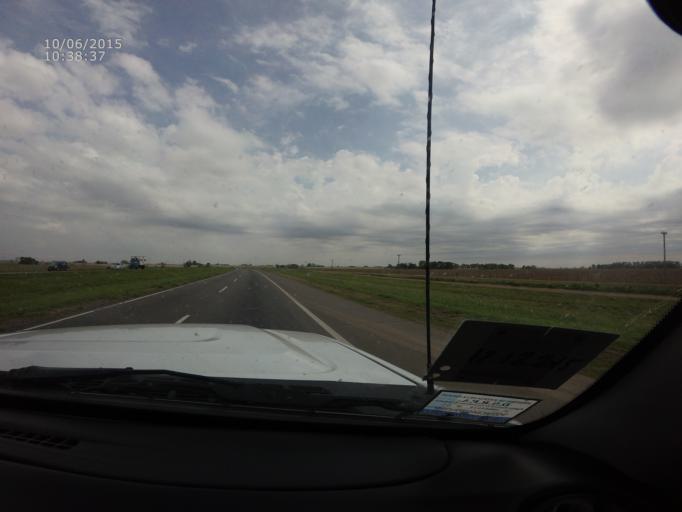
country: AR
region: Buenos Aires
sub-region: Partido de Ramallo
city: Ramallo
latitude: -33.5317
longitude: -60.1106
